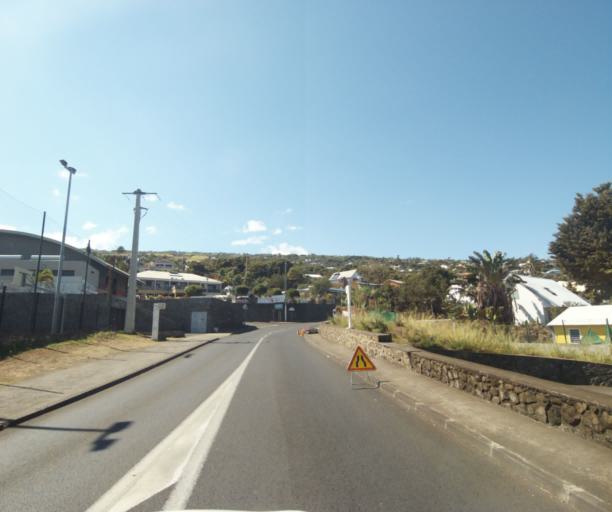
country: RE
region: Reunion
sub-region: Reunion
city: Saint-Paul
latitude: -20.9912
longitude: 55.3300
